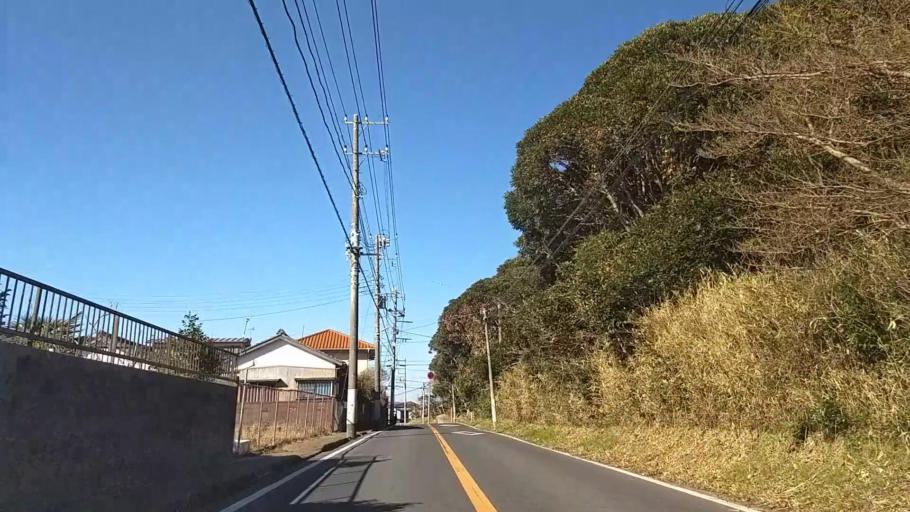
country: JP
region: Chiba
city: Hasaki
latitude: 35.7318
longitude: 140.8551
